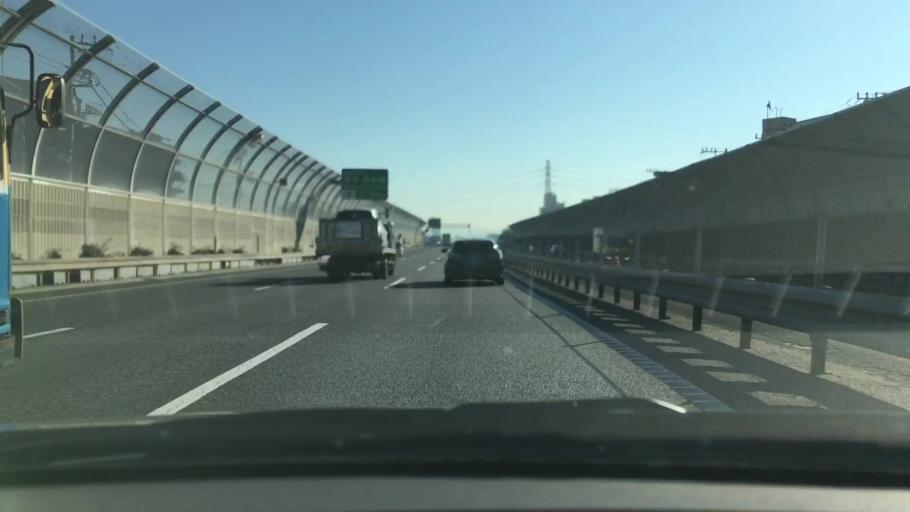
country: JP
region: Chiba
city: Funabashi
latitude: 35.7056
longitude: 139.9448
